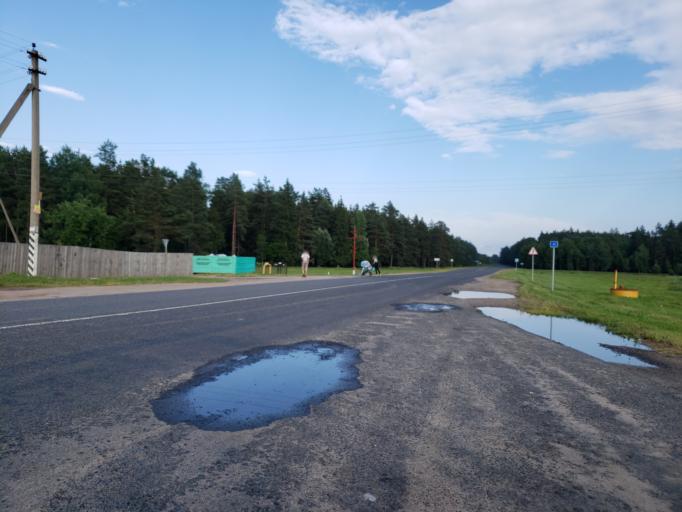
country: BY
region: Minsk
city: Chervyen'
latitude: 53.6963
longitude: 28.4540
